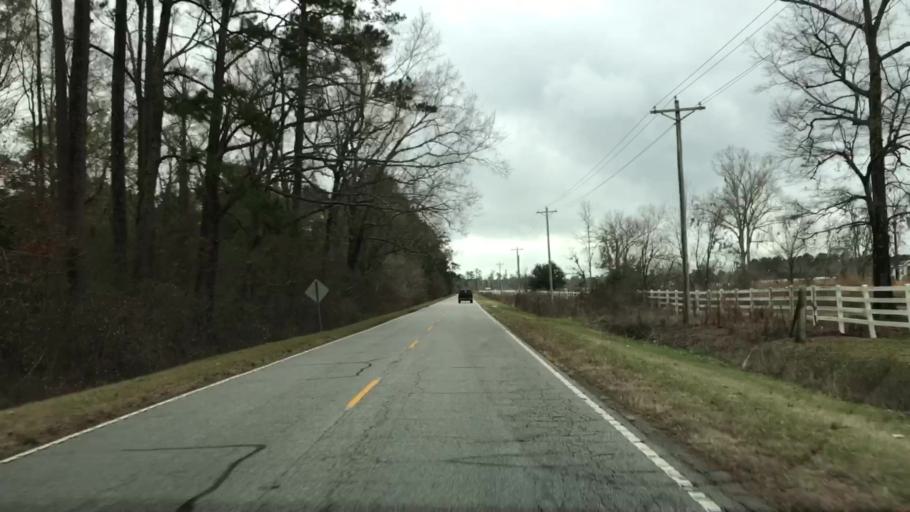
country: US
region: South Carolina
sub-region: Florence County
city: Johnsonville
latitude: 33.6573
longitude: -79.4191
